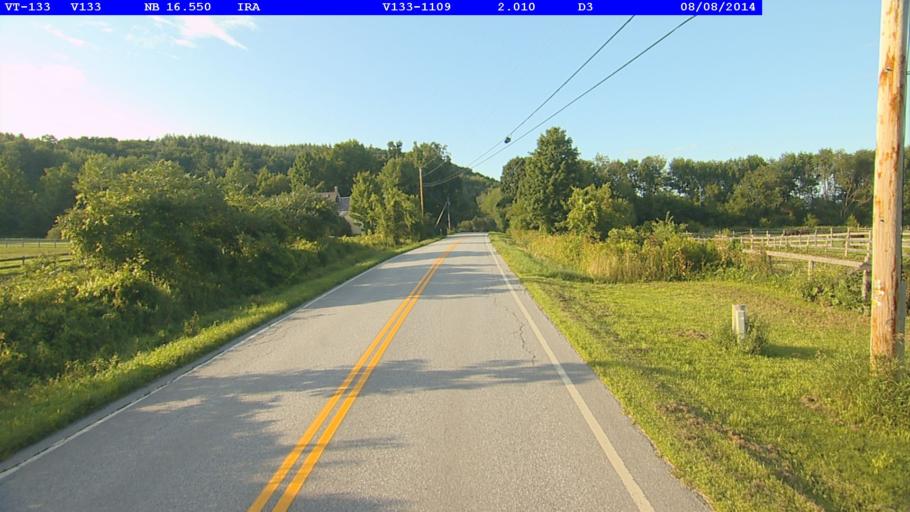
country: US
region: Vermont
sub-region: Rutland County
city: West Rutland
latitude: 43.5227
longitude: -73.0711
